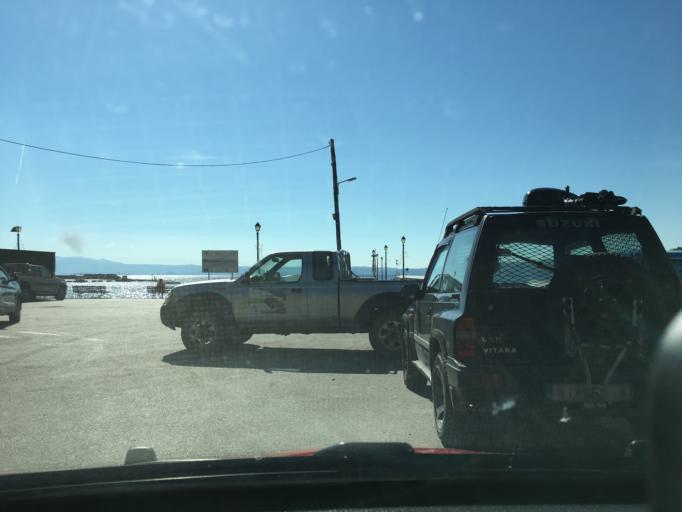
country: GR
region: Central Macedonia
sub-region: Nomos Chalkidikis
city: Agios Nikolaos
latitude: 40.3363
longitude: 23.7202
